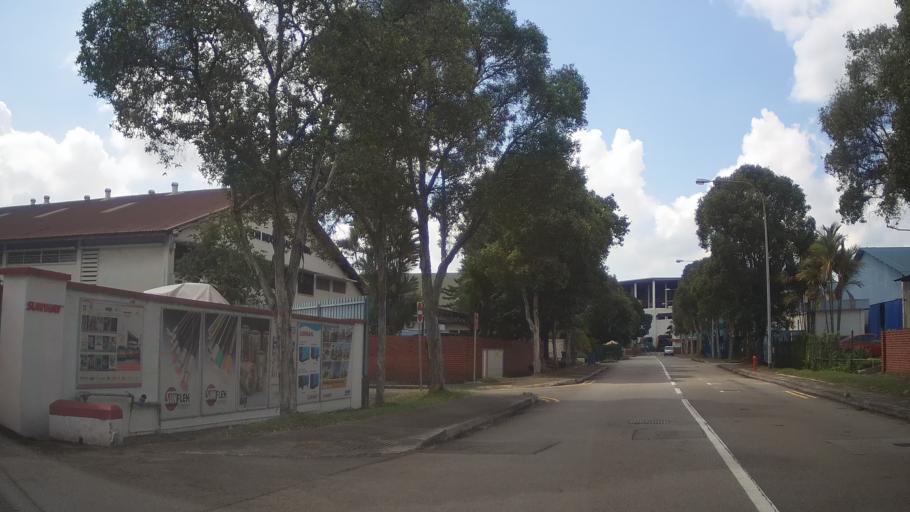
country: MY
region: Johor
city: Johor Bahru
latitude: 1.3187
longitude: 103.6655
